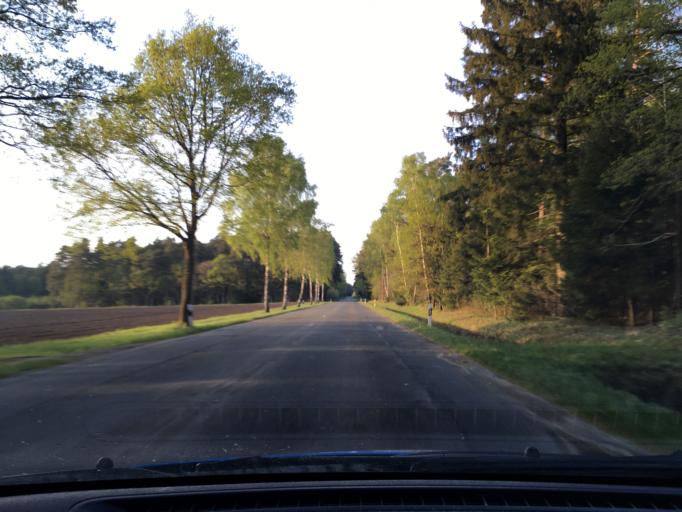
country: DE
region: Lower Saxony
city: Wietzendorf
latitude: 52.9701
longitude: 9.9801
